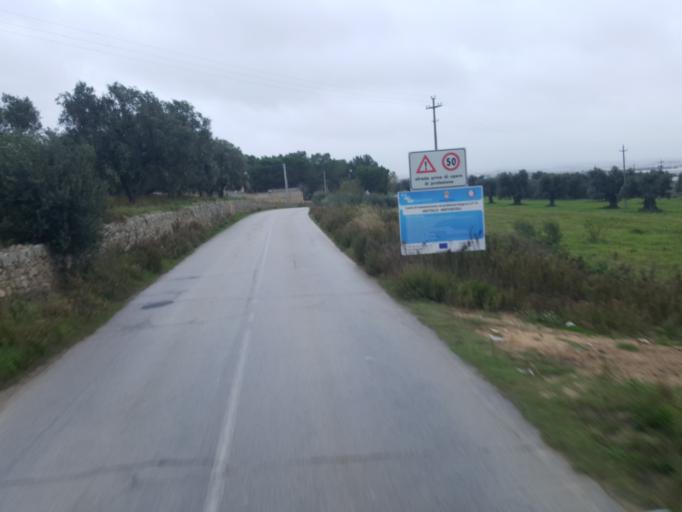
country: IT
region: Apulia
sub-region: Provincia di Taranto
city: Montemesola
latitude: 40.5493
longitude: 17.3525
